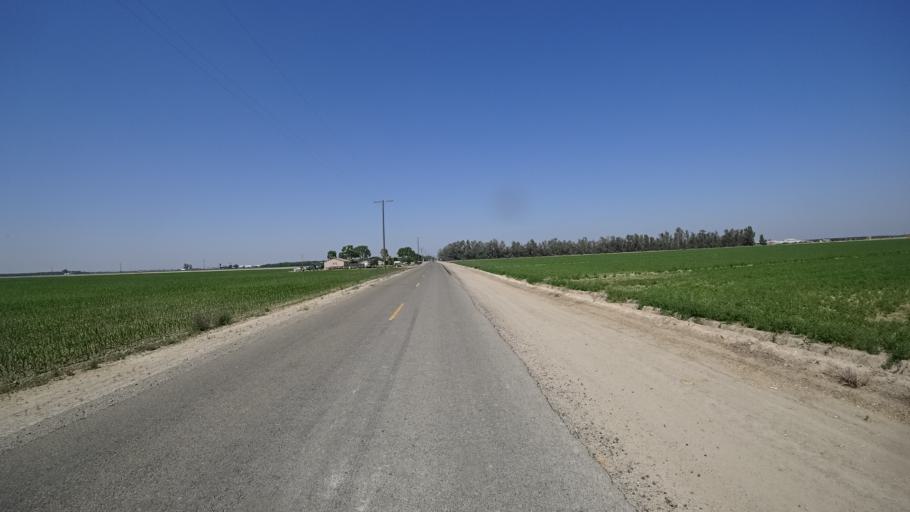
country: US
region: California
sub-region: Tulare County
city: Goshen
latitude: 36.3722
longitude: -119.5338
